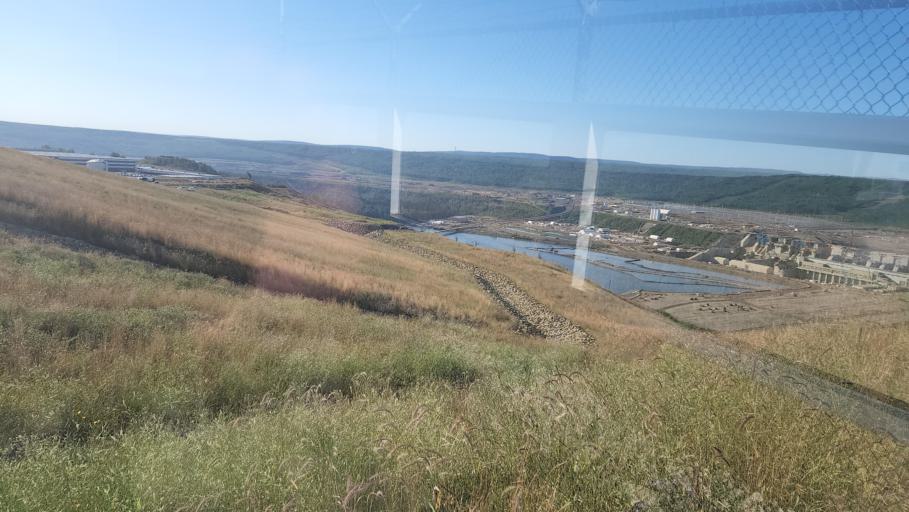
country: CA
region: British Columbia
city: Fort St. John
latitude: 56.2047
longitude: -120.9087
